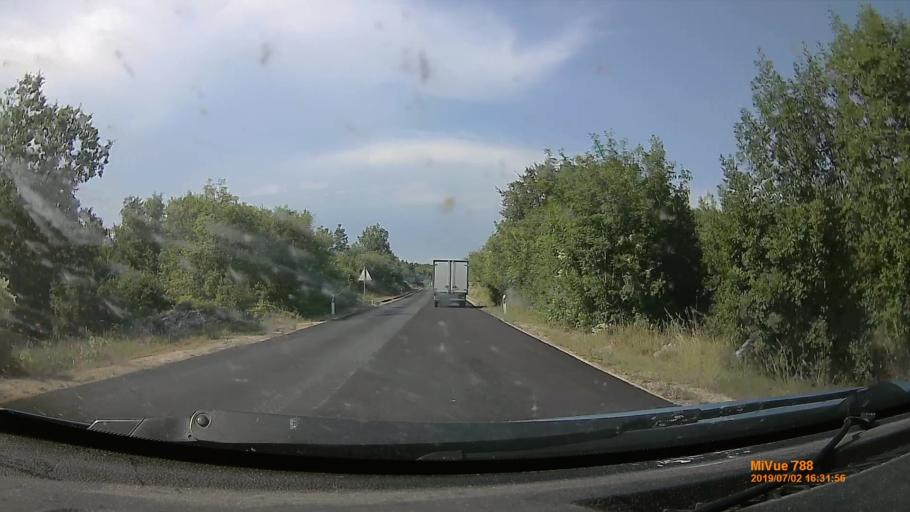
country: HR
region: Primorsko-Goranska
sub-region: Grad Krk
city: Krk
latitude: 45.0588
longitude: 14.4876
